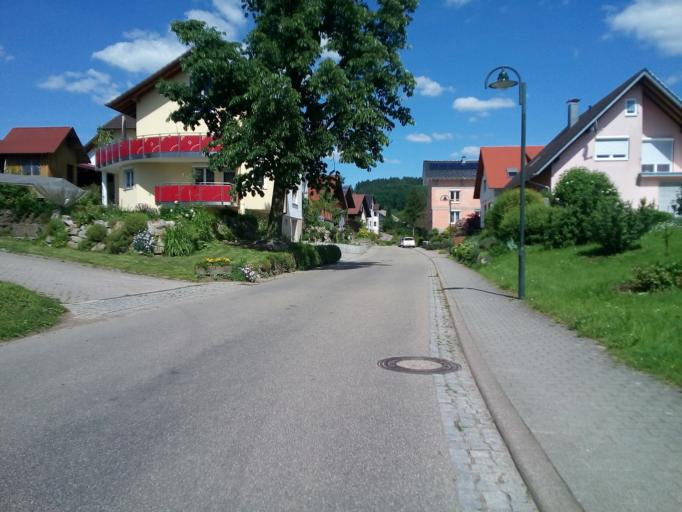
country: DE
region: Baden-Wuerttemberg
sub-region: Freiburg Region
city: Haslach
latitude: 48.5821
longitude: 8.0602
